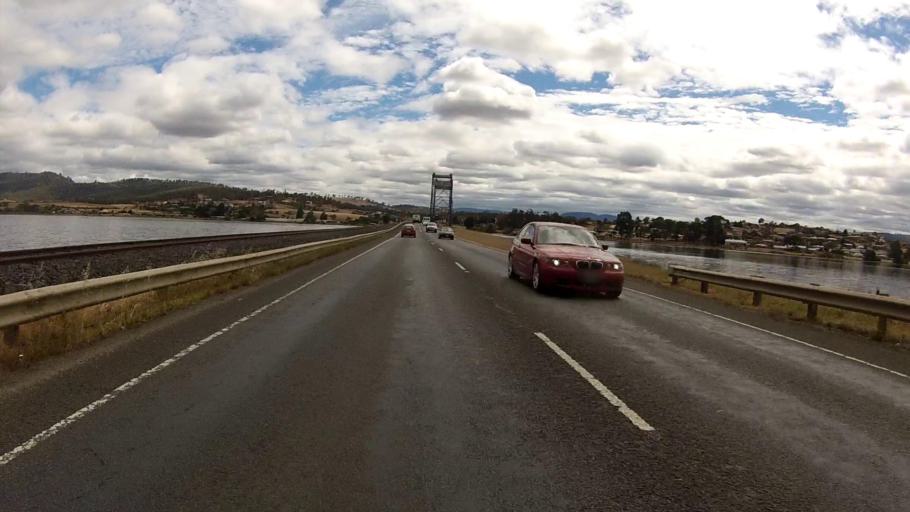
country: AU
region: Tasmania
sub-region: Glenorchy
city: Granton
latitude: -42.7446
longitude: 147.2250
